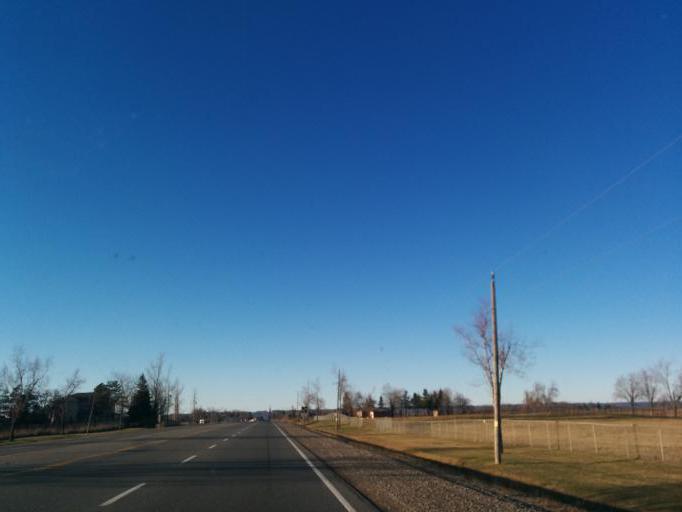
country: CA
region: Ontario
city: Brampton
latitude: 43.7876
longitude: -79.8972
